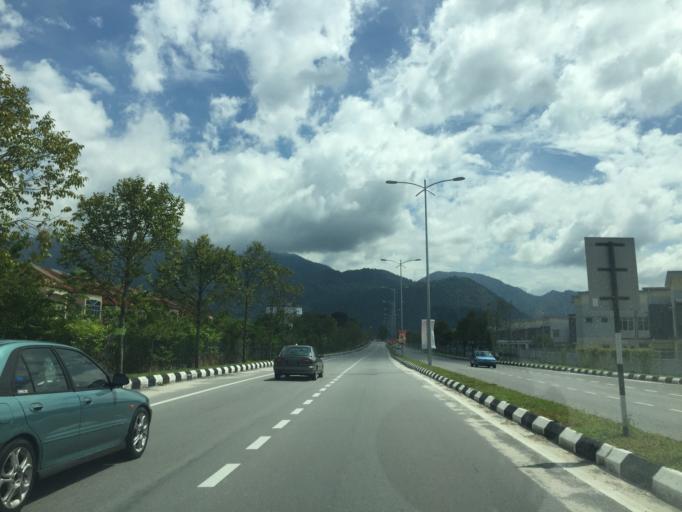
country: MY
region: Perak
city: Kampar
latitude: 4.3280
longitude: 101.1339
